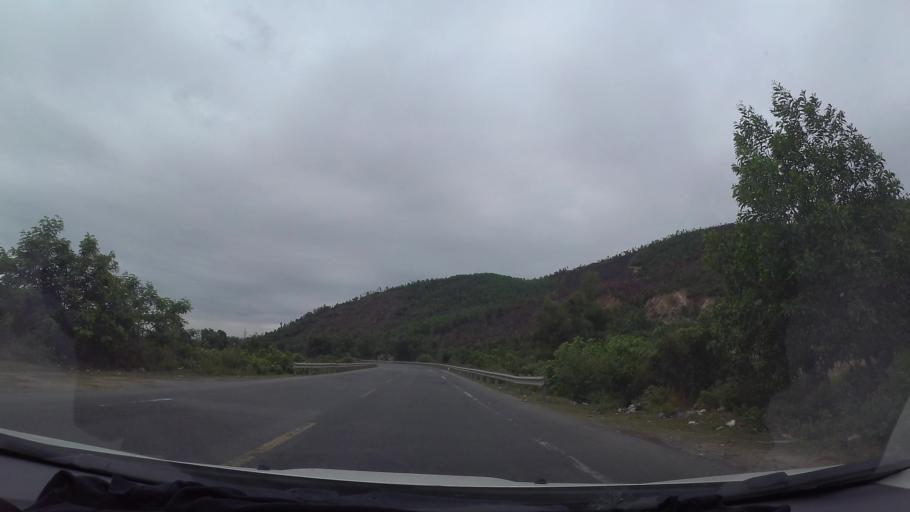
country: VN
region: Da Nang
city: Lien Chieu
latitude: 16.1232
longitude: 108.1001
